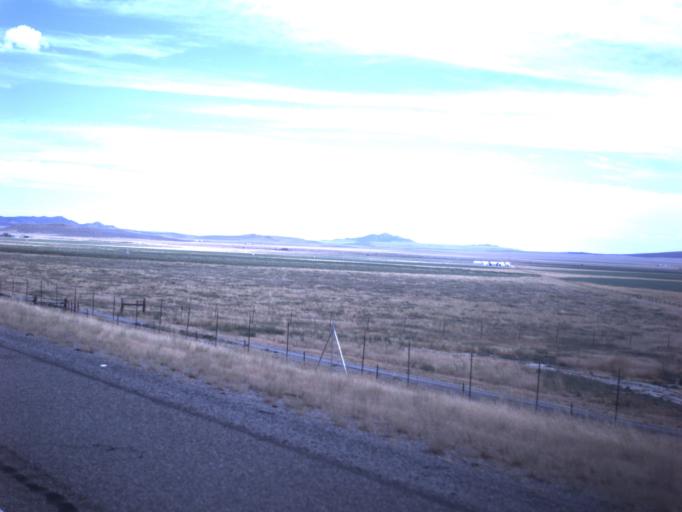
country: US
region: Idaho
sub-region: Oneida County
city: Malad City
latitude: 41.9911
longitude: -112.8245
